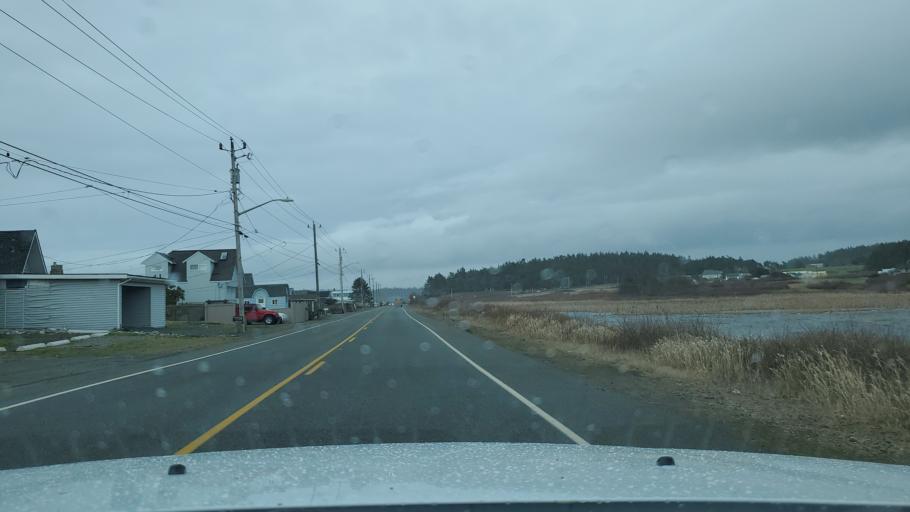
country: US
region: Washington
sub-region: Island County
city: Ault Field
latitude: 48.3049
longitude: -122.7209
